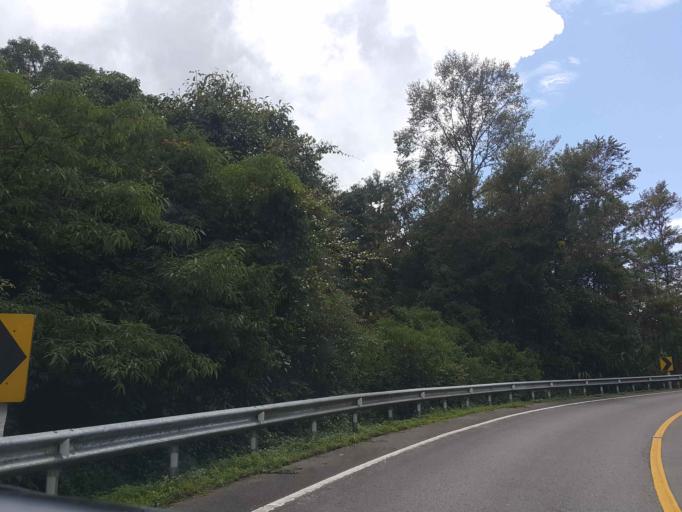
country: TH
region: Chiang Mai
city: Mae Chaem
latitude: 18.5300
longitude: 98.4950
